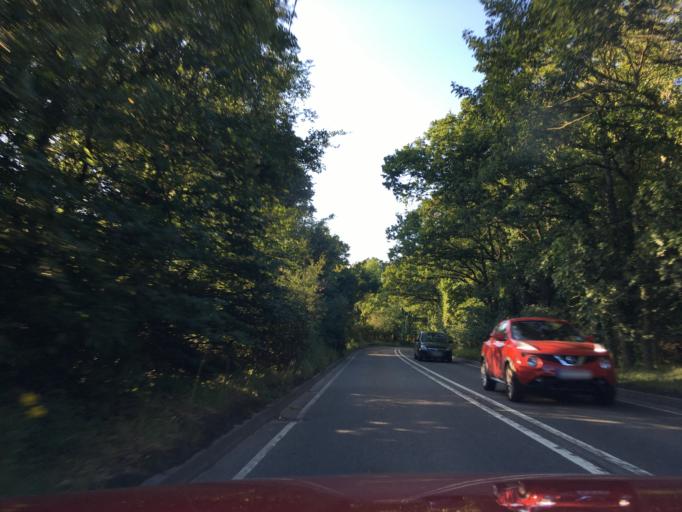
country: GB
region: England
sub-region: Hampshire
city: Tadley
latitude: 51.3729
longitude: -1.1512
